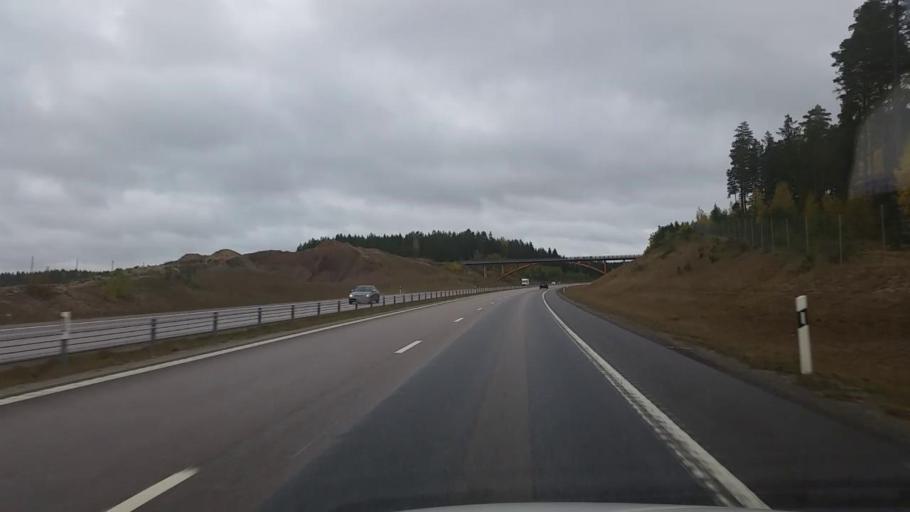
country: SE
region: Uppsala
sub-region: Osthammars Kommun
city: Bjorklinge
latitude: 60.1179
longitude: 17.5488
